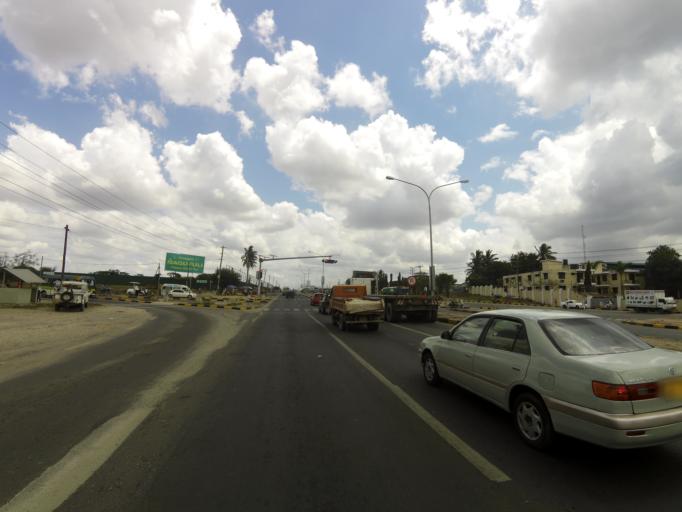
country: TZ
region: Dar es Salaam
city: Dar es Salaam
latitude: -6.8579
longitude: 39.2180
